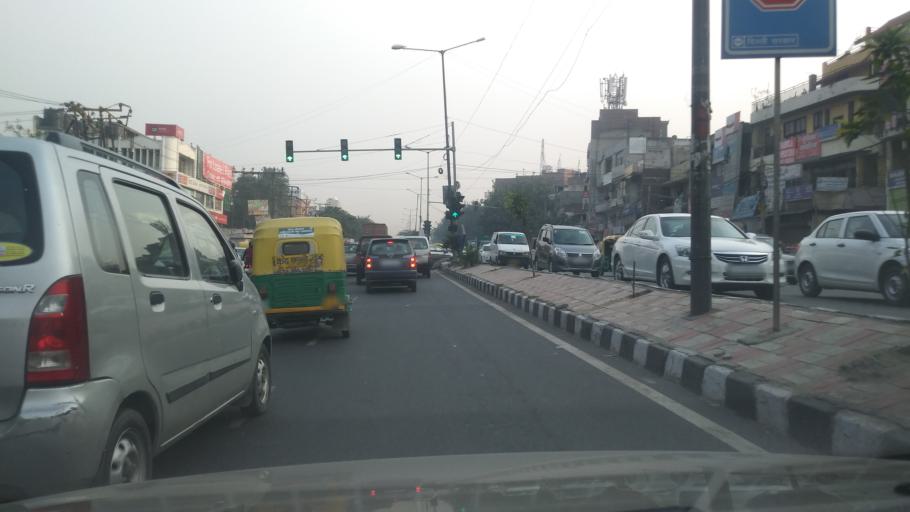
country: IN
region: Uttar Pradesh
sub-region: Gautam Buddha Nagar
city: Noida
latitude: 28.5373
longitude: 77.2672
